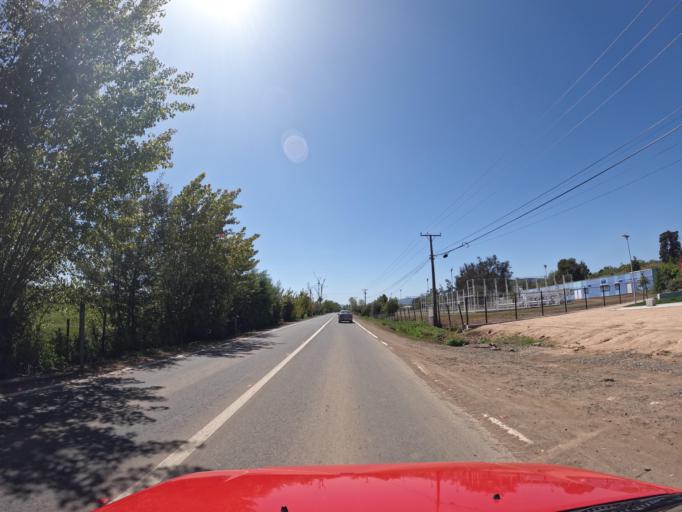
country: CL
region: Maule
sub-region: Provincia de Linares
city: Colbun
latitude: -35.7618
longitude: -71.4208
